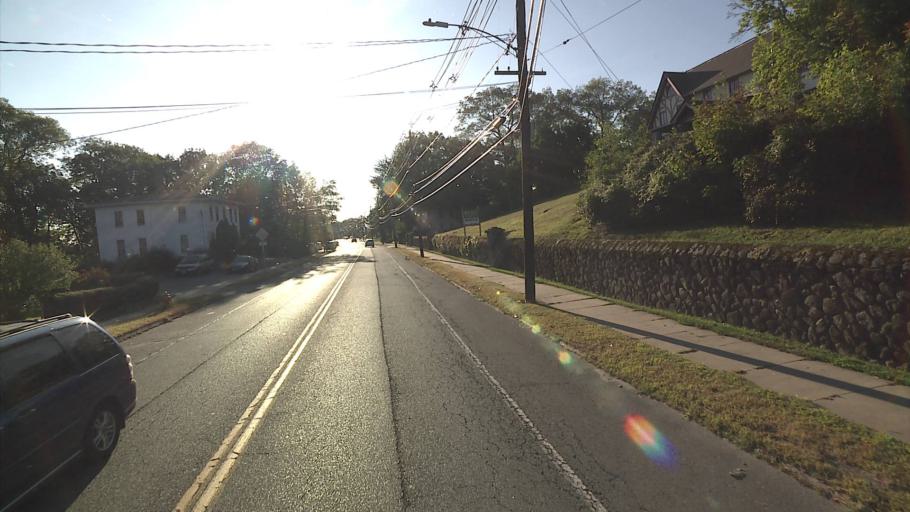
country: US
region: Connecticut
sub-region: Windham County
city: Willimantic
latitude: 41.7096
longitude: -72.2133
